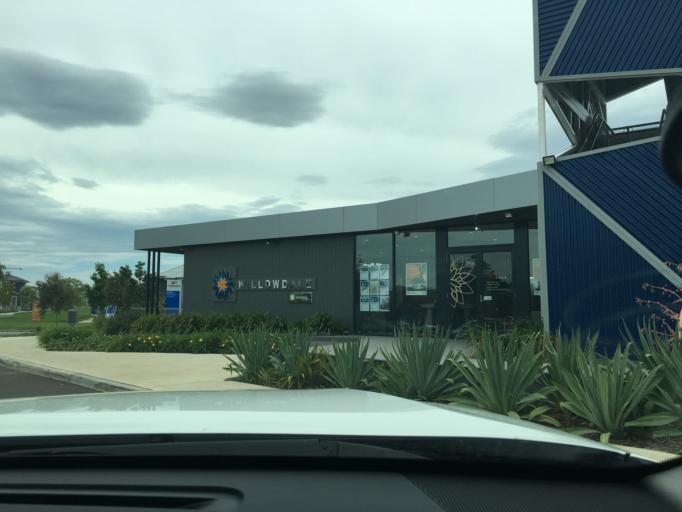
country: AU
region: New South Wales
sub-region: Campbelltown Municipality
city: Denham Court
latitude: -33.9773
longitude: 150.8116
